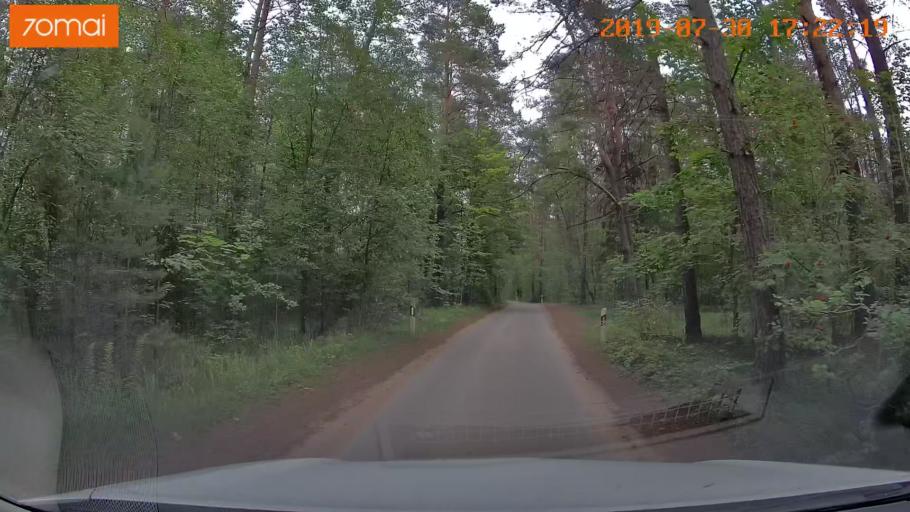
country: LT
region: Vilnius County
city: Rasos
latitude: 54.7434
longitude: 25.3923
